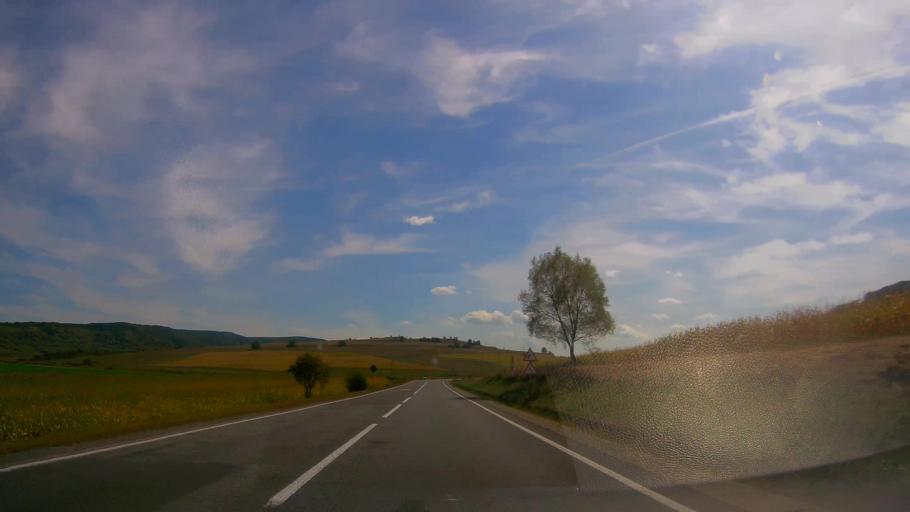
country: RO
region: Mures
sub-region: Comuna Nades
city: Nades
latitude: 46.3140
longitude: 24.7223
